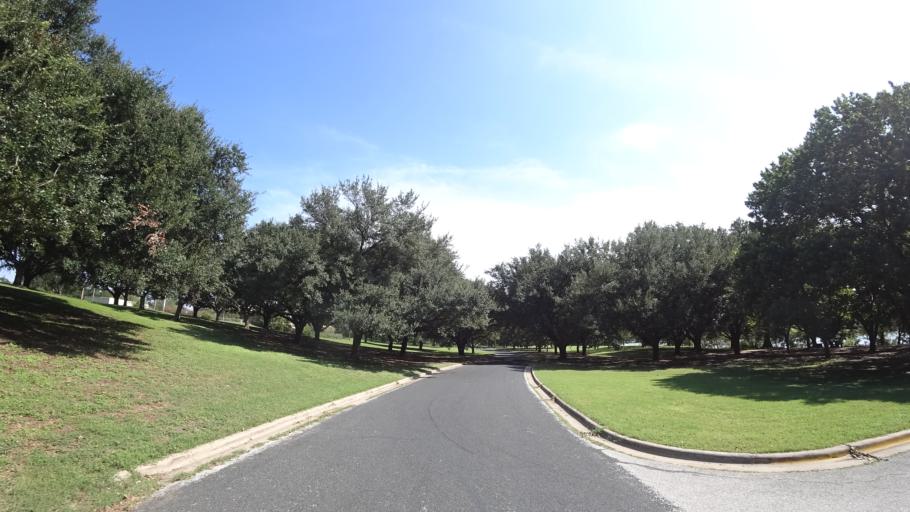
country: US
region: Texas
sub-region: Travis County
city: Austin
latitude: 30.2504
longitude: -97.7318
